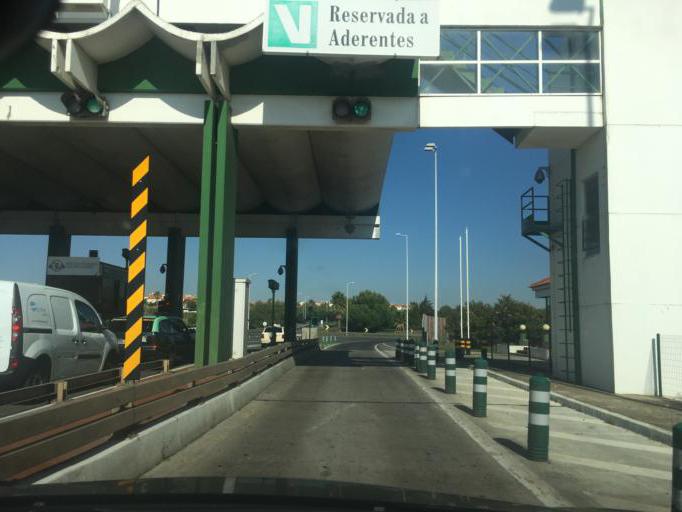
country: PT
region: Lisbon
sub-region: Oeiras
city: Porto Salvo
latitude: 38.7115
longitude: -9.3016
